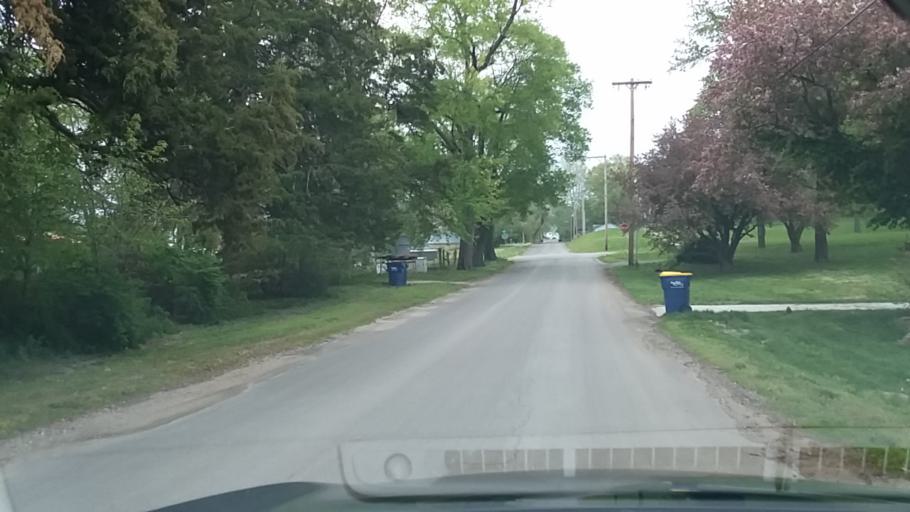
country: US
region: Kansas
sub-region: Douglas County
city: Eudora
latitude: 38.9482
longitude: -95.0999
